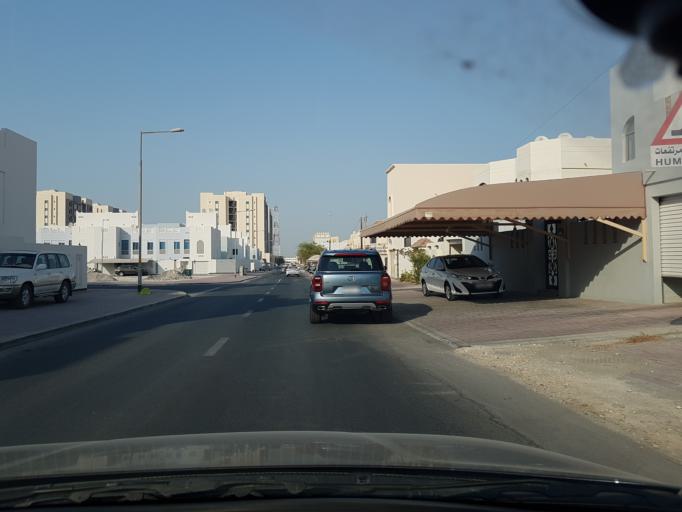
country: BH
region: Northern
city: Ar Rifa'
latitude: 26.1315
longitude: 50.5814
